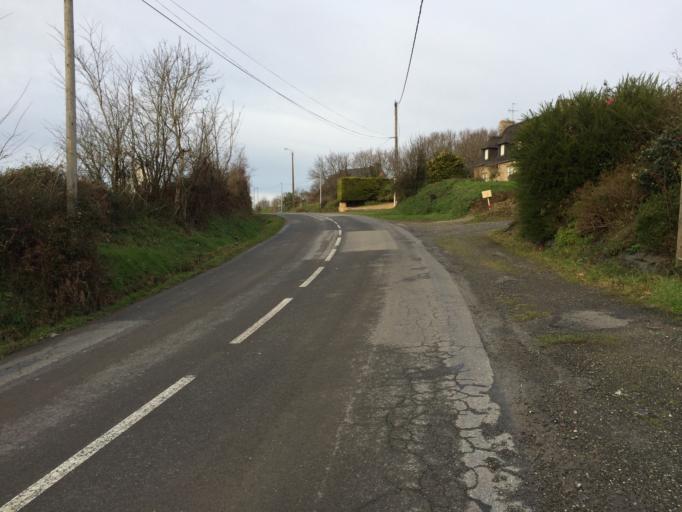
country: FR
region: Brittany
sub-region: Departement du Finistere
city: Daoulas
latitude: 48.3684
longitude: -4.2561
